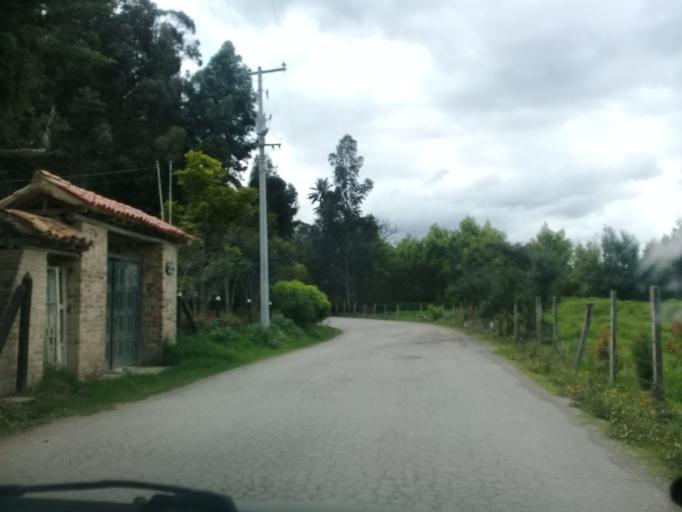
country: CO
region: Cundinamarca
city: Tenjo
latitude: 4.8570
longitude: -74.2010
